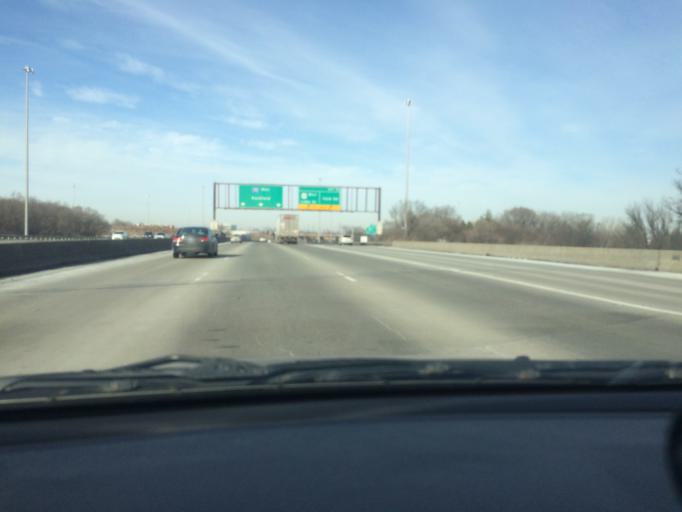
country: US
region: Illinois
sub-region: DuPage County
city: Elmhurst
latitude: 41.9142
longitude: -87.9390
